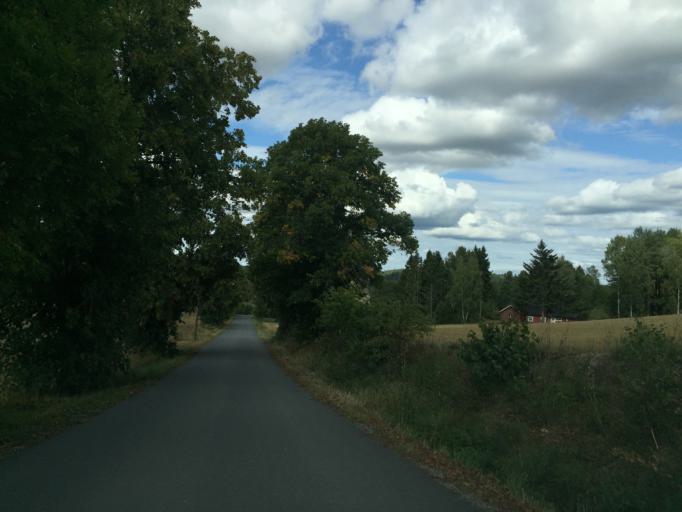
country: NO
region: Ostfold
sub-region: Hobol
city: Elvestad
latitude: 59.6022
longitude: 10.9225
